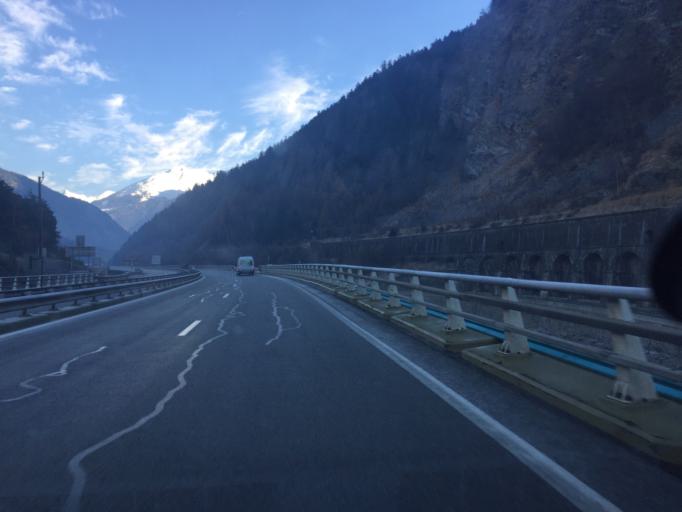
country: FR
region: Rhone-Alpes
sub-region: Departement de la Savoie
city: Modane
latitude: 45.1997
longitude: 6.6005
